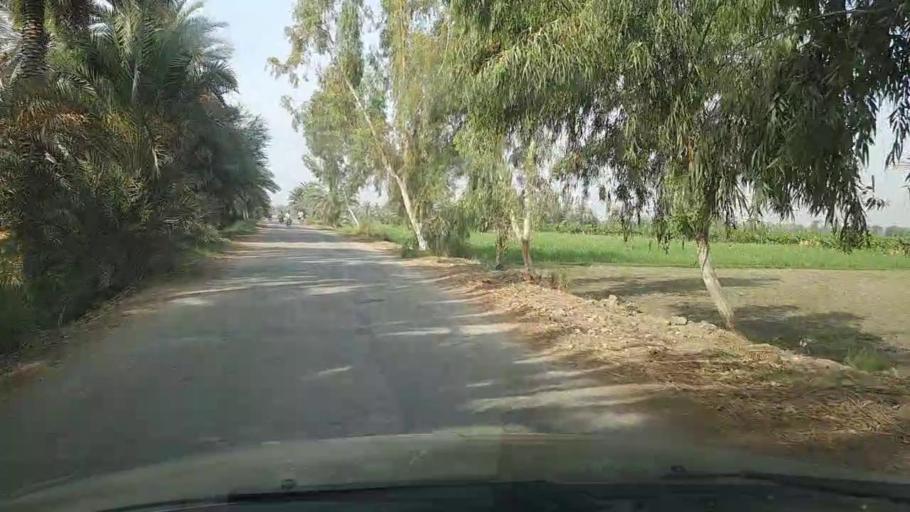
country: PK
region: Sindh
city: Pir jo Goth
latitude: 27.5515
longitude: 68.5326
